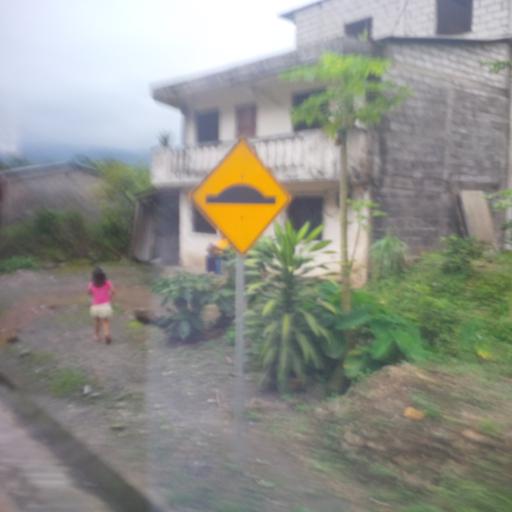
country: EC
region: Chimborazo
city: Alausi
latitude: -2.1984
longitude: -79.1148
